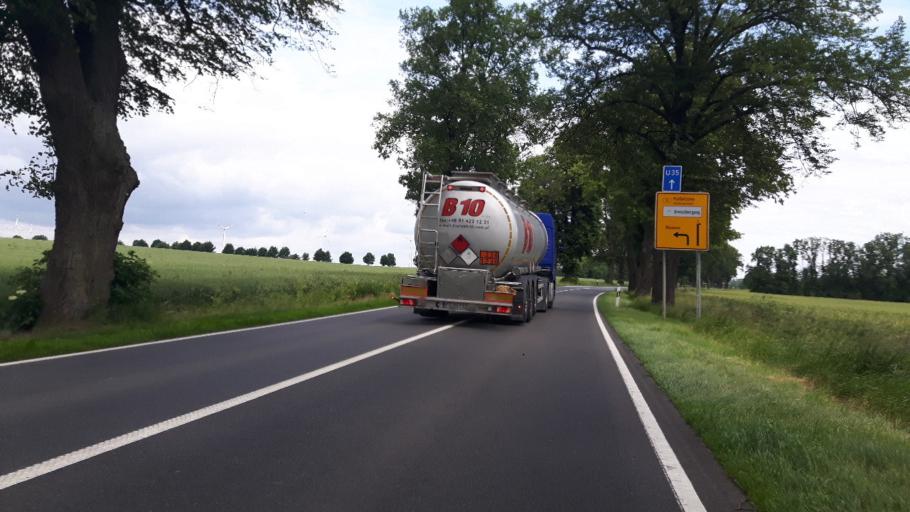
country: PL
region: West Pomeranian Voivodeship
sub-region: Powiat policki
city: Kolbaskowo
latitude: 53.3028
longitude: 14.4075
